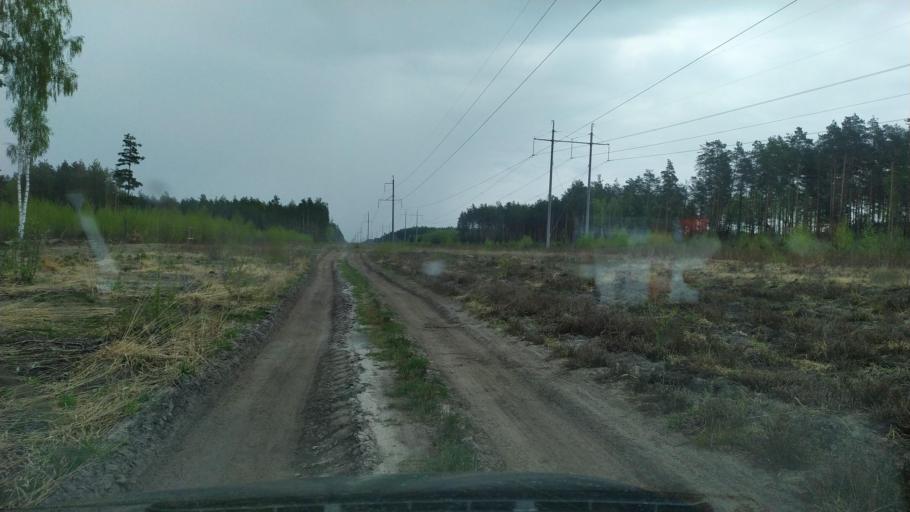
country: BY
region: Brest
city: Pruzhany
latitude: 52.3619
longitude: 24.5934
